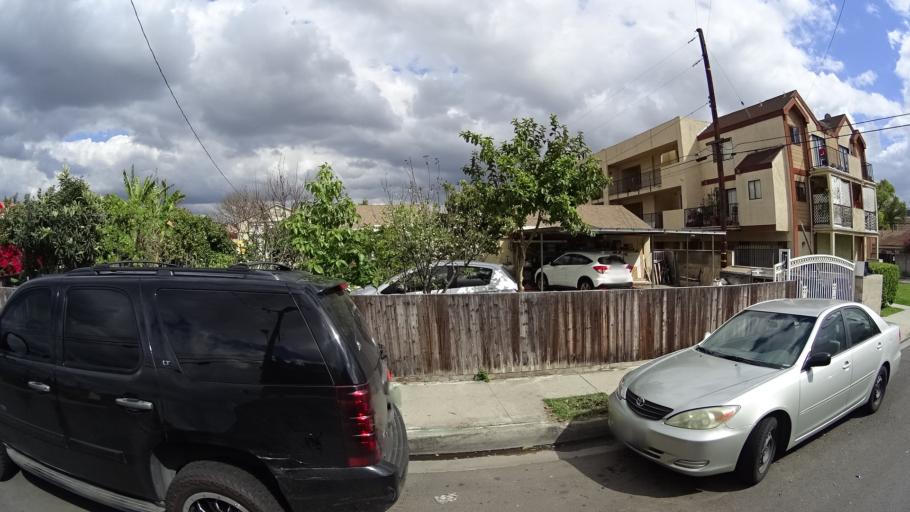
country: US
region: California
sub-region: Los Angeles County
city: Baldwin Park
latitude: 34.0891
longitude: -117.9670
